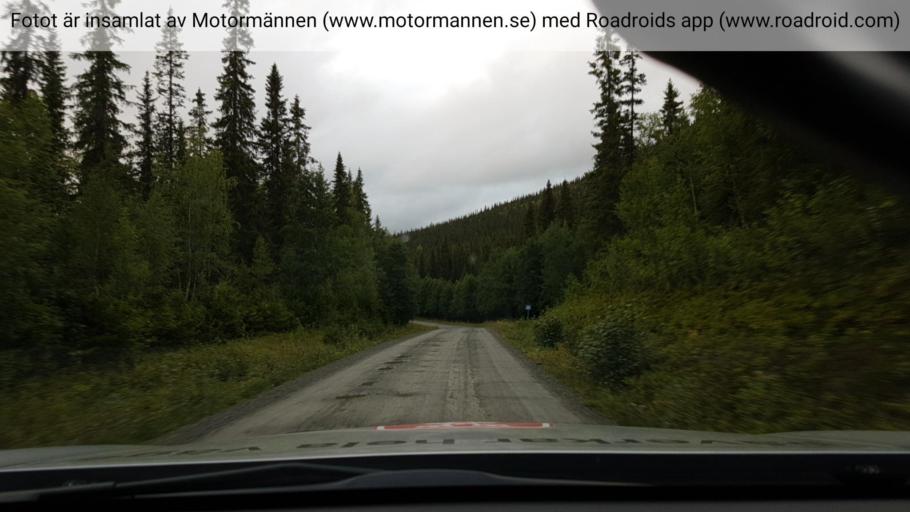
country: SE
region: Vaesterbotten
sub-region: Vilhelmina Kommun
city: Sjoberg
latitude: 65.5113
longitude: 15.4689
